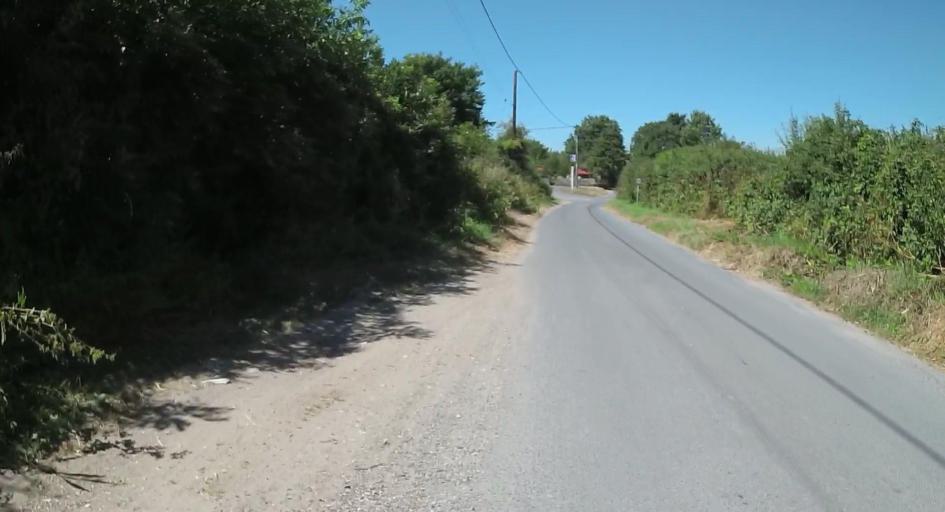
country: GB
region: England
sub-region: Dorset
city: Bovington Camp
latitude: 50.6503
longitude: -2.2975
